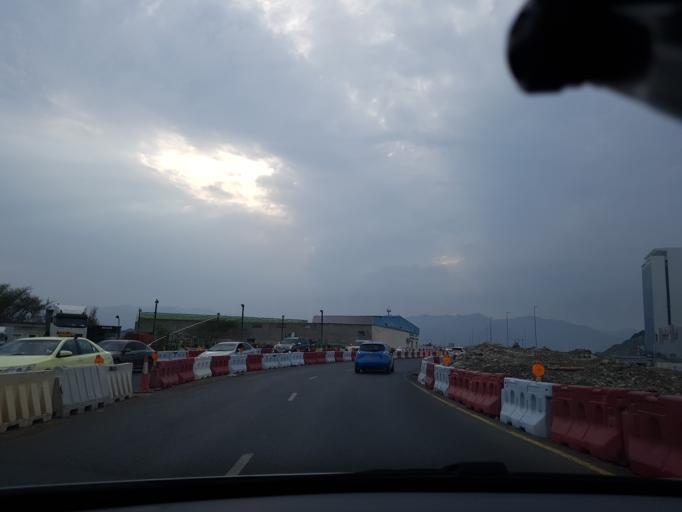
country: AE
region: Al Fujayrah
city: Al Fujayrah
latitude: 25.1221
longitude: 56.3198
